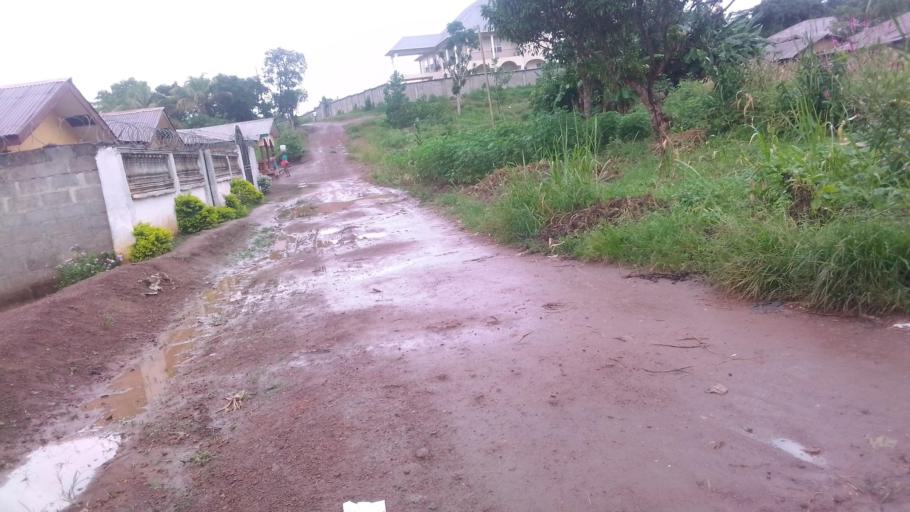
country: SL
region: Eastern Province
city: Kenema
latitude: 7.8507
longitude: -11.1834
